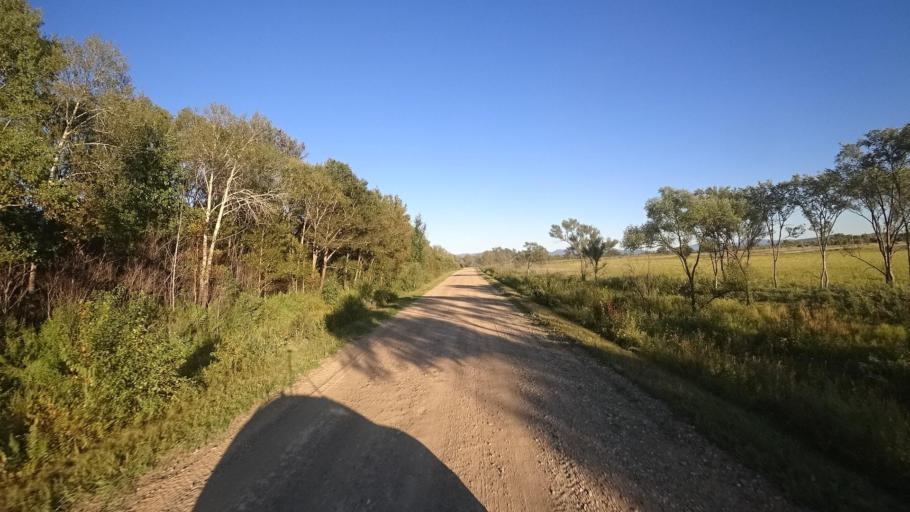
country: RU
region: Primorskiy
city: Kirovskiy
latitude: 44.8275
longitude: 133.5916
